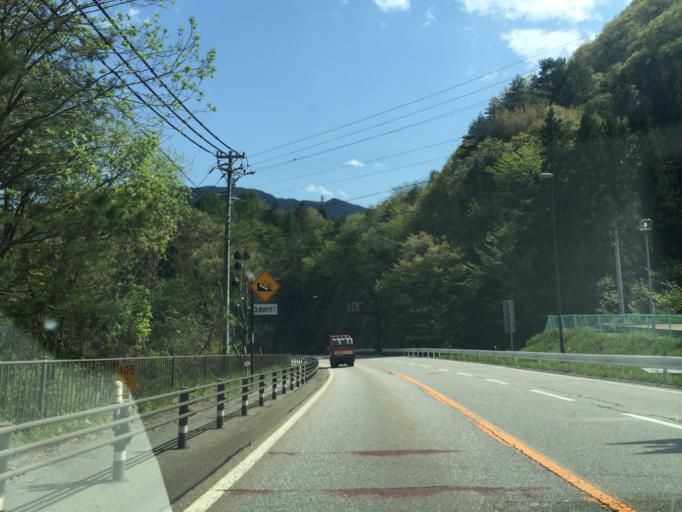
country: JP
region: Nagano
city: Iida
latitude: 35.4317
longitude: 137.7001
